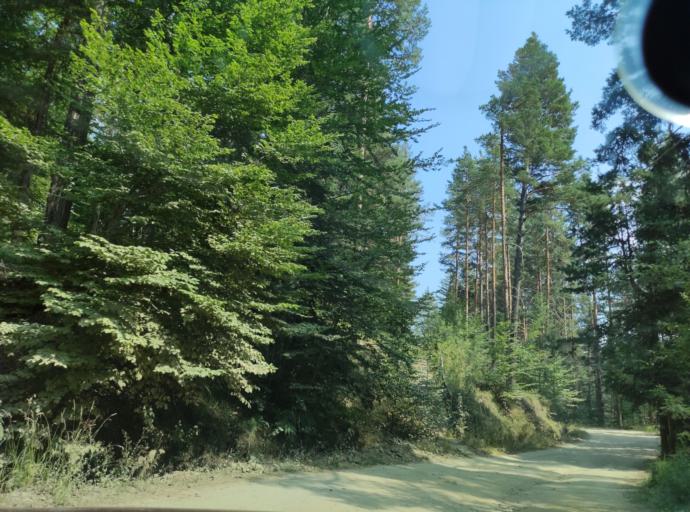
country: BG
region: Blagoevgrad
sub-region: Obshtina Belitsa
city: Belitsa
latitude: 42.0253
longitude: 23.5804
